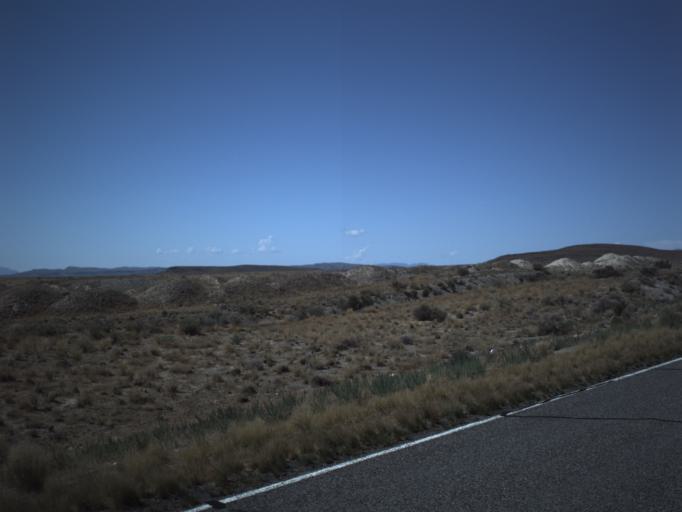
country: US
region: Utah
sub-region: Beaver County
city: Milford
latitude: 39.0588
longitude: -113.2502
